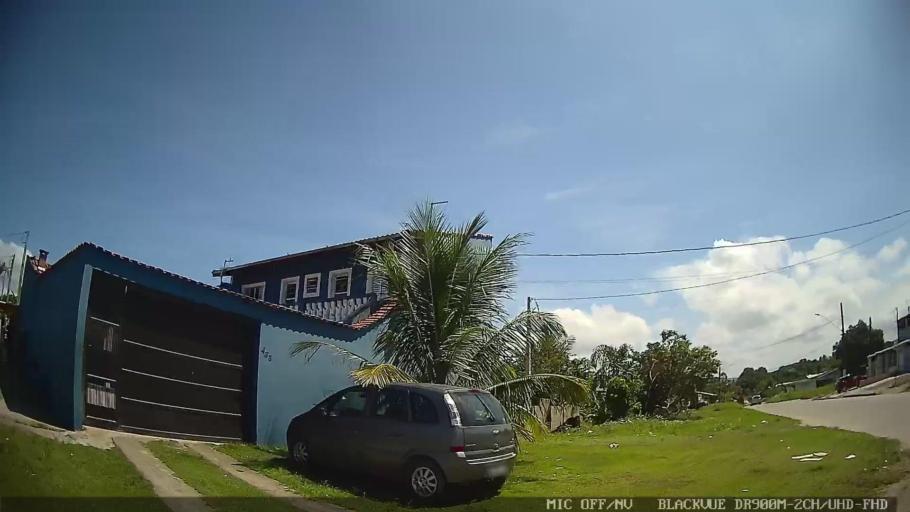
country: BR
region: Sao Paulo
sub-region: Peruibe
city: Peruibe
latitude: -24.2985
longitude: -46.9899
